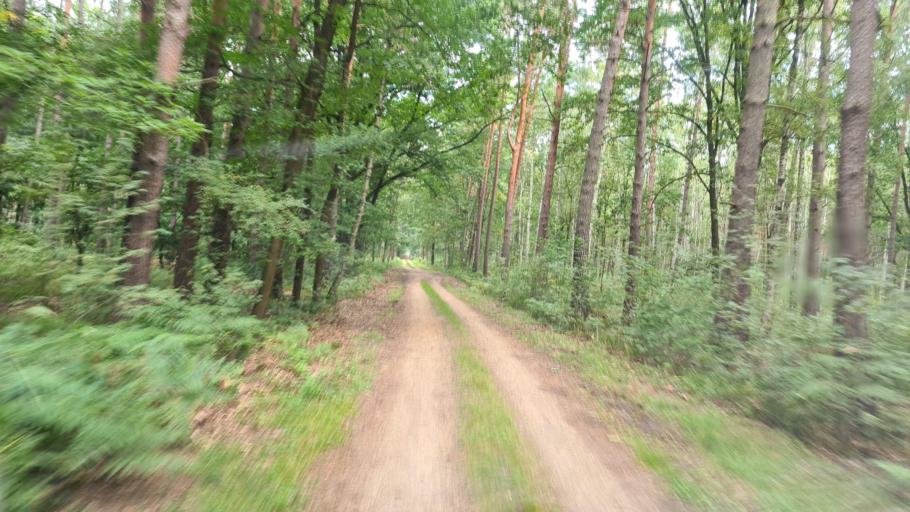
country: DE
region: Brandenburg
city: Hohenbucko
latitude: 51.7925
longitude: 13.5349
